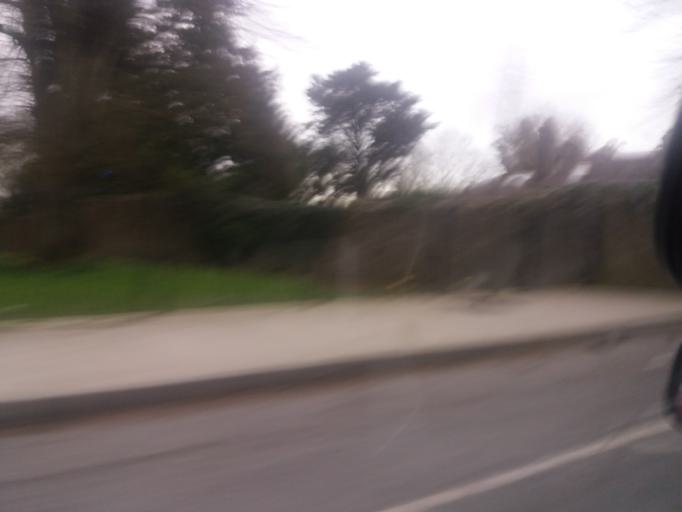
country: IE
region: Munster
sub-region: County Limerick
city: Adare
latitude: 52.5599
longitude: -8.7949
